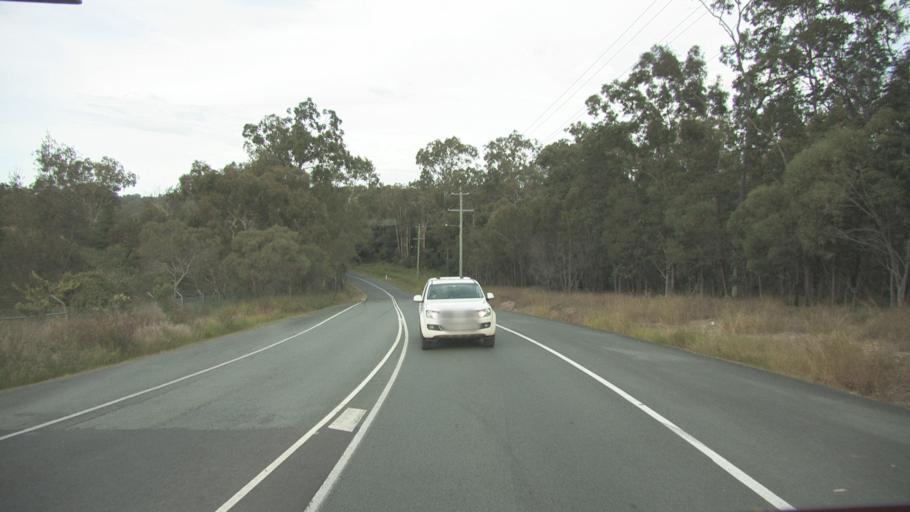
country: AU
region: Queensland
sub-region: Logan
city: Beenleigh
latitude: -27.7136
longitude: 153.1703
